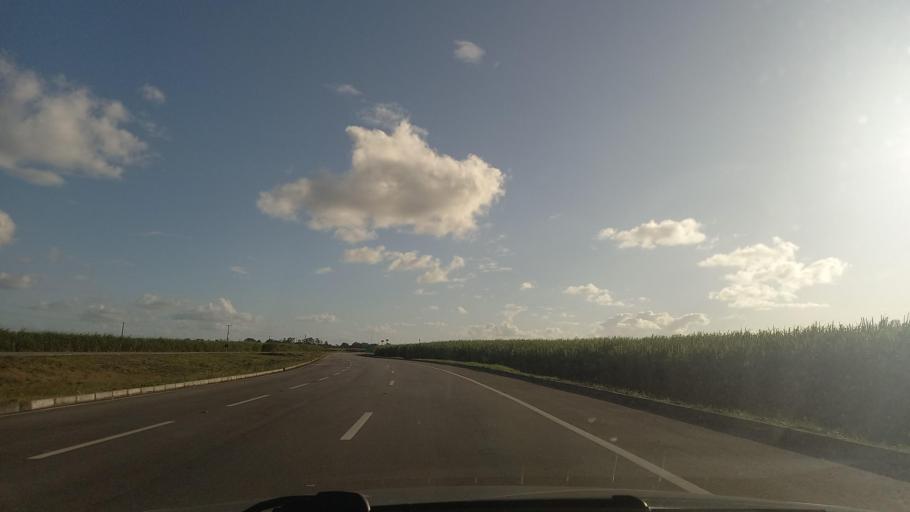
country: BR
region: Alagoas
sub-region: Sao Miguel Dos Campos
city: Sao Miguel dos Campos
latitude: -9.8022
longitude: -36.1973
